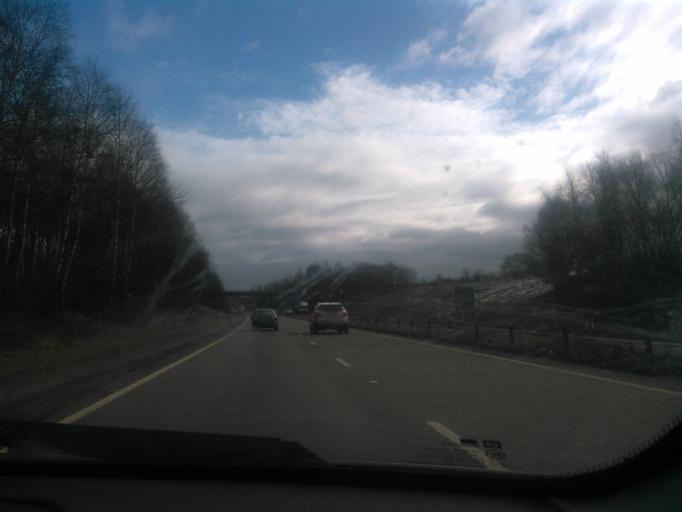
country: GB
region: England
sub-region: Staffordshire
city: Uttoxeter
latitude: 52.8982
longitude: -1.7905
